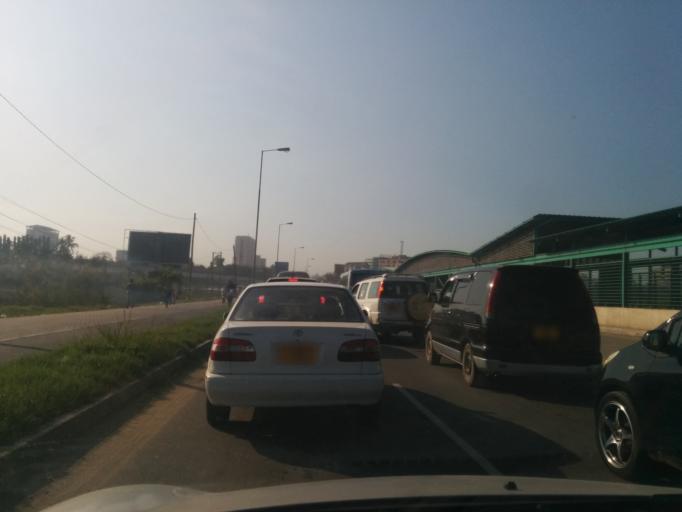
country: TZ
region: Dar es Salaam
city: Dar es Salaam
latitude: -6.8112
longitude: 39.2689
